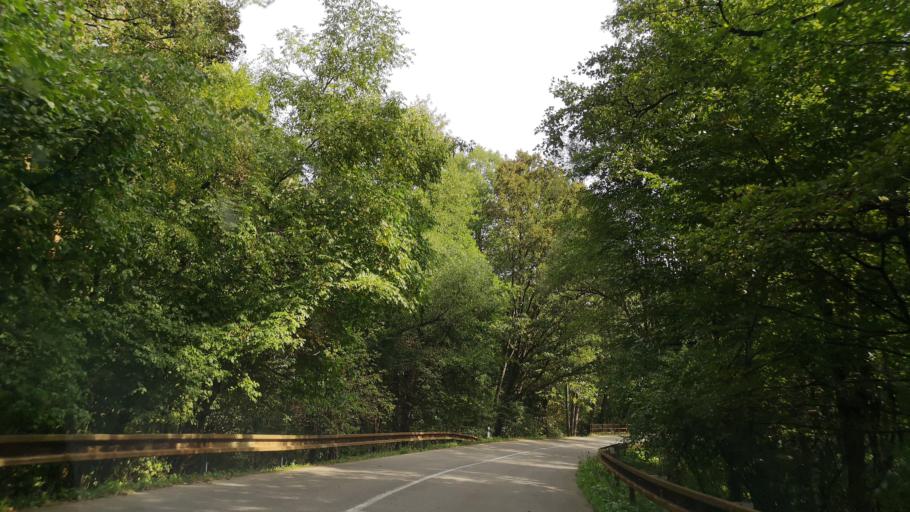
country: SK
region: Banskobystricky
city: Revuca
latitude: 48.6059
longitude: 20.1719
